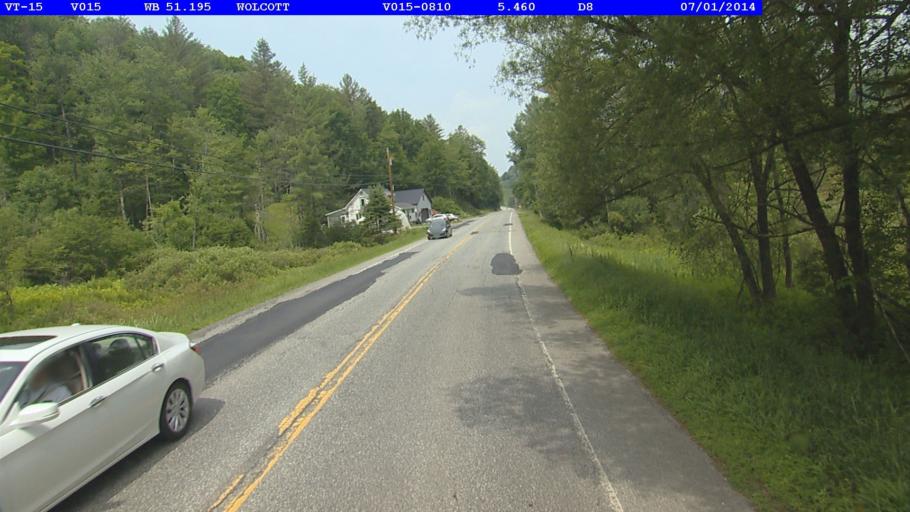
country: US
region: Vermont
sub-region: Caledonia County
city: Hardwick
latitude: 44.5347
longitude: -72.4435
